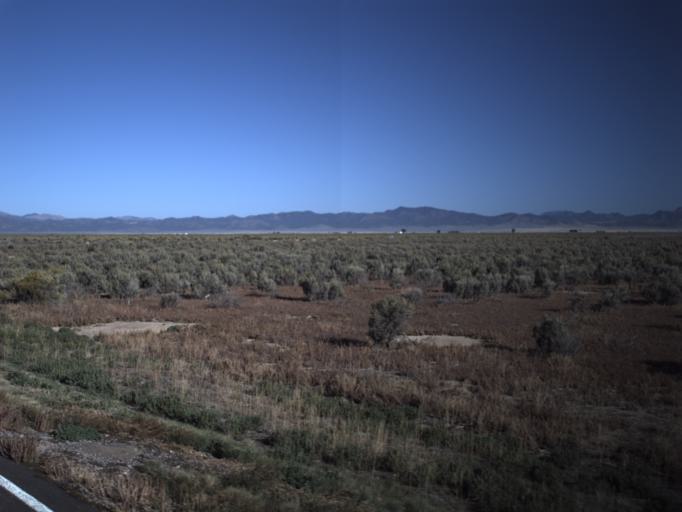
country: US
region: Utah
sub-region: Washington County
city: Enterprise
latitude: 37.7290
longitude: -113.7104
